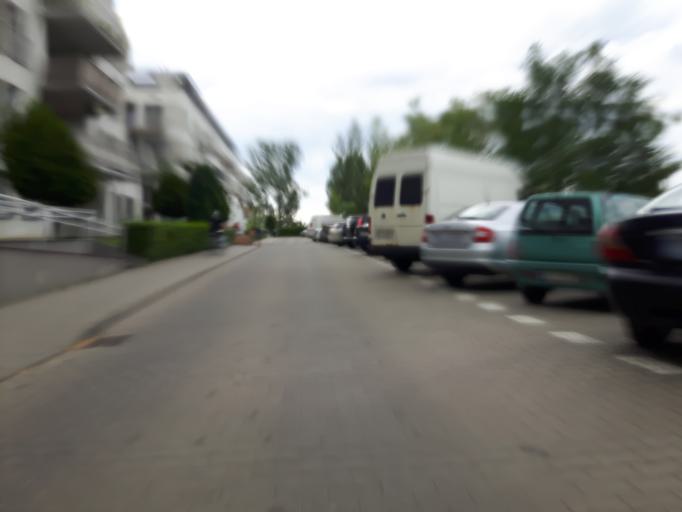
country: PL
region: Masovian Voivodeship
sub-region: Powiat wolominski
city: Zabki
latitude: 52.2782
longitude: 21.1045
